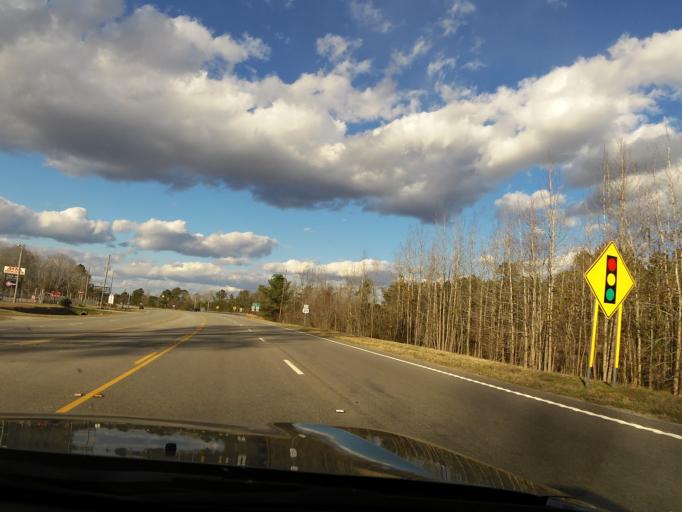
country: US
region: South Carolina
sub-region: Clarendon County
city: Manning
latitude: 33.7183
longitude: -80.1962
